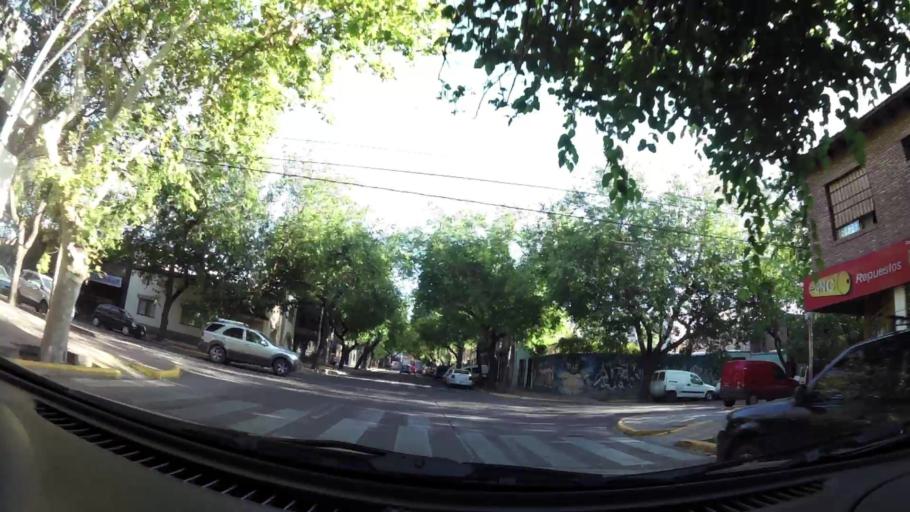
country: AR
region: Mendoza
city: Mendoza
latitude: -32.9030
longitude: -68.8384
